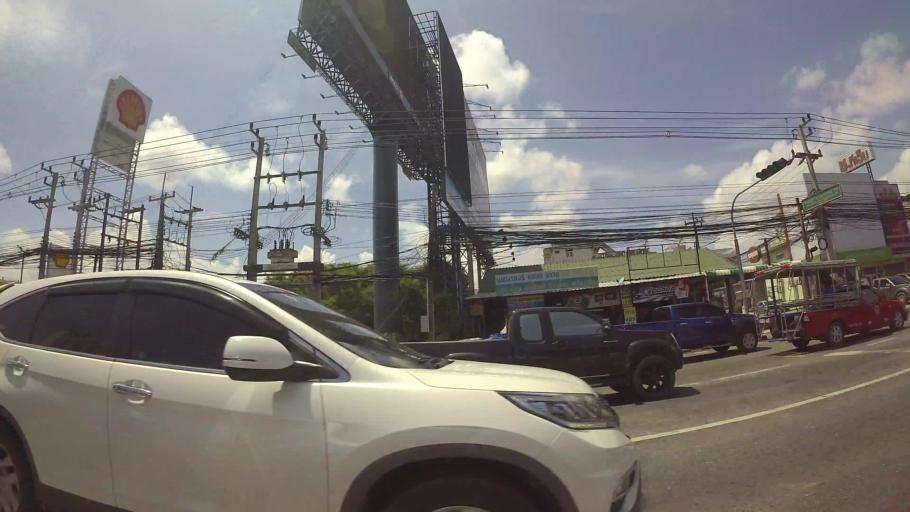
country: TH
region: Rayong
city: Rayong
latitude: 12.6828
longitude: 101.2611
